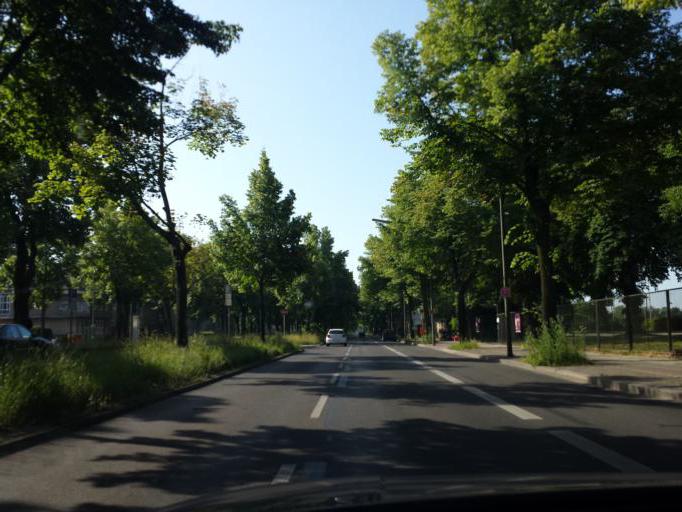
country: DE
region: Berlin
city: Mariendorf
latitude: 52.4302
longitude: 13.3921
